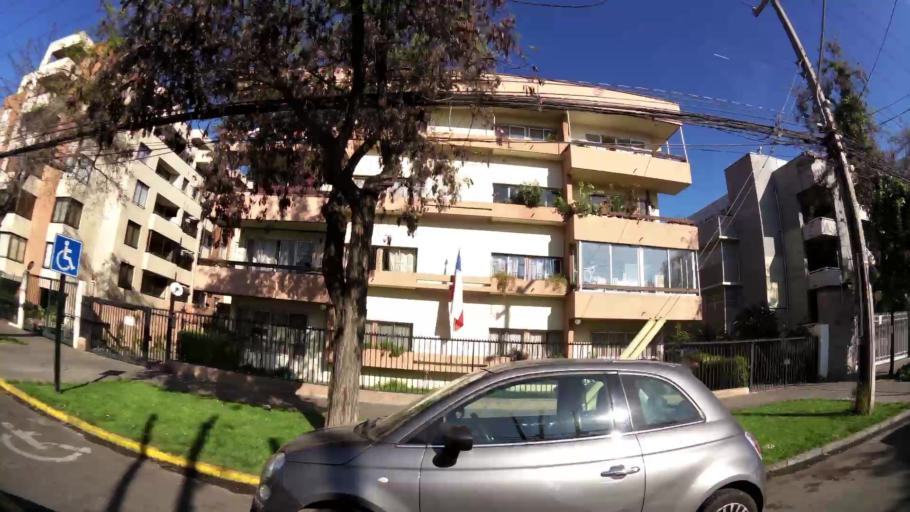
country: CL
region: Santiago Metropolitan
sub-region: Provincia de Santiago
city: Villa Presidente Frei, Nunoa, Santiago, Chile
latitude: -33.4532
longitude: -70.5918
